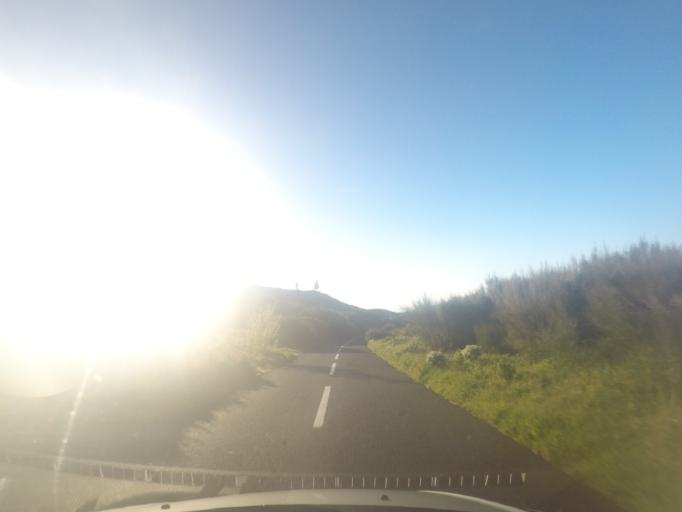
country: PT
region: Madeira
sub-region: Funchal
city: Nossa Senhora do Monte
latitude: 32.7204
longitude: -16.9103
